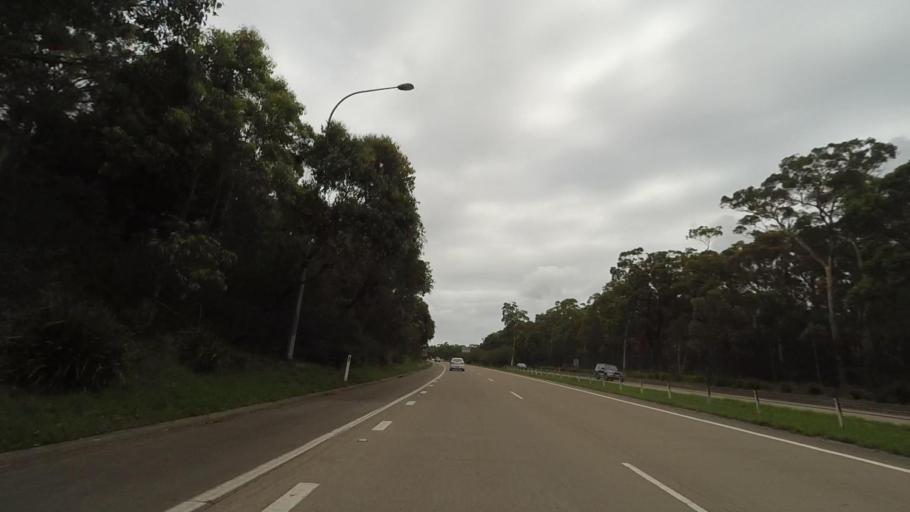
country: AU
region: New South Wales
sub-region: Lake Macquarie Shire
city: Cardiff South
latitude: -32.9638
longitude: 151.6763
